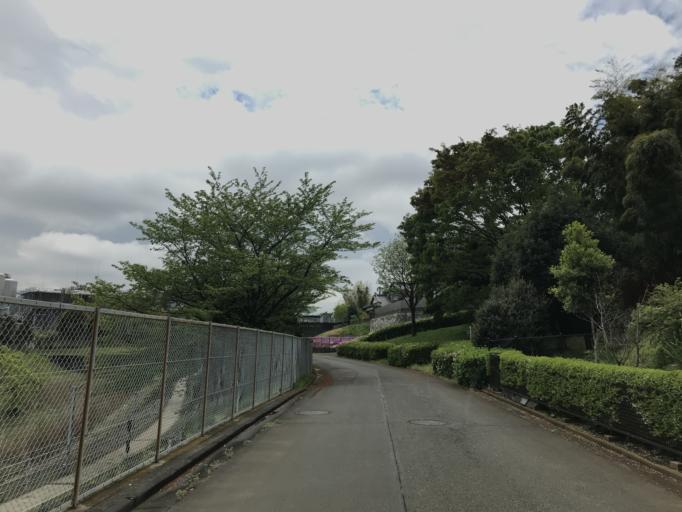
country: JP
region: Ibaraki
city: Moriya
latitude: 35.9511
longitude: 139.9636
